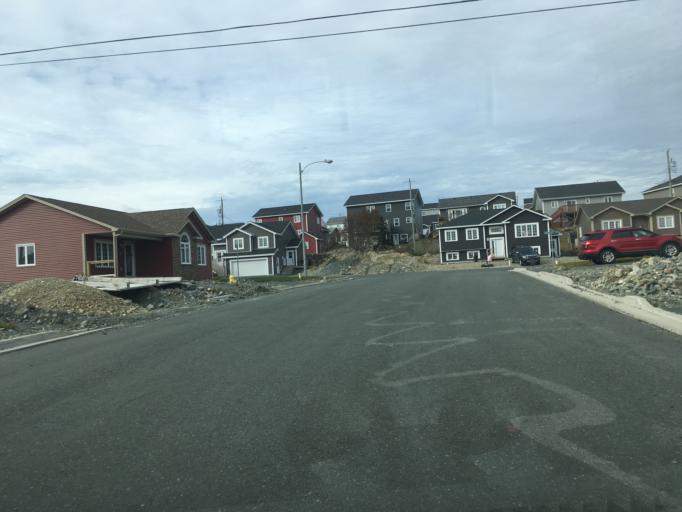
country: CA
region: Newfoundland and Labrador
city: Mount Pearl
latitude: 47.5501
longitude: -52.7853
